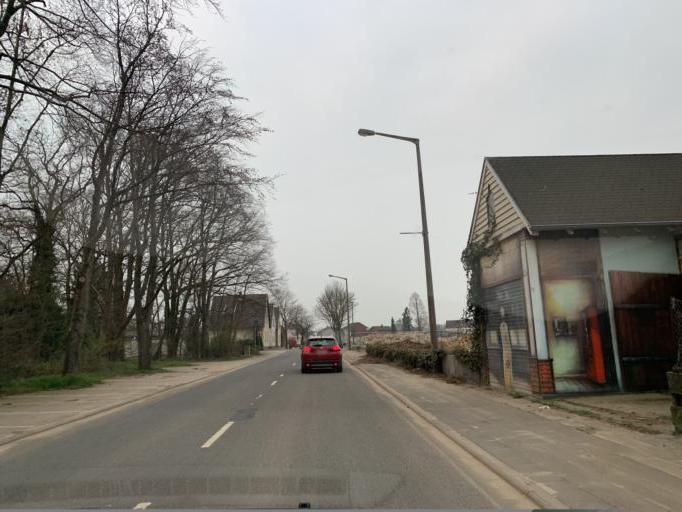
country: DE
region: North Rhine-Westphalia
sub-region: Regierungsbezirk Koln
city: Elsdorf
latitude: 50.8867
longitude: 6.5943
